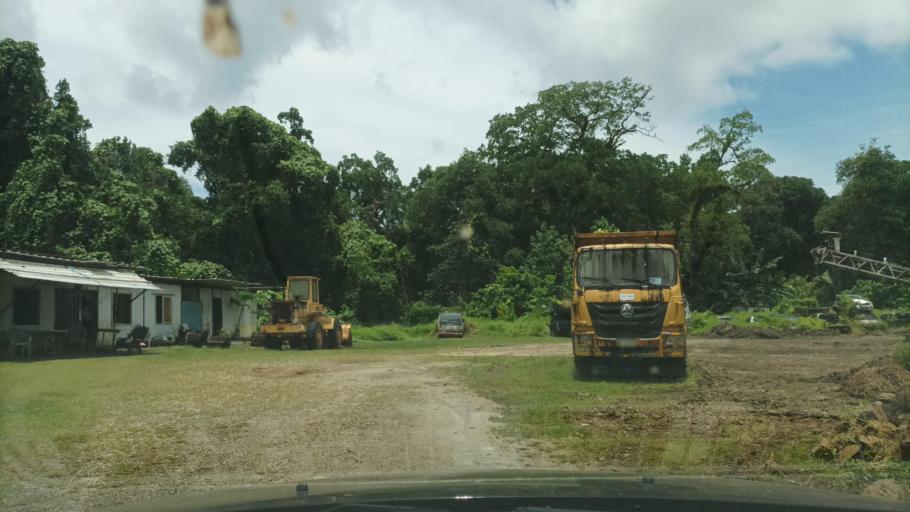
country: FM
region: Kosrae
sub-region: Lelu Municipality
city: Tofol
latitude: 5.3233
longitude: 163.0128
